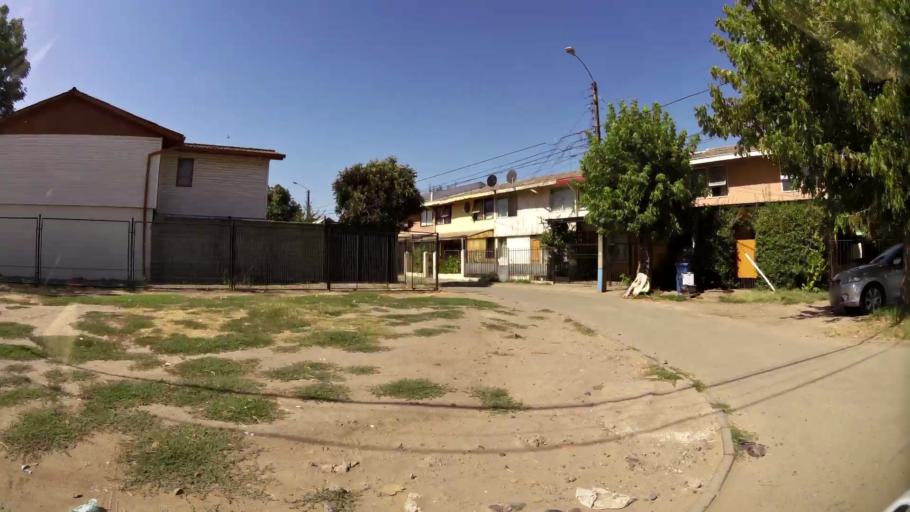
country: CL
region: Maule
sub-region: Provincia de Talca
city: Talca
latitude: -35.4368
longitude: -71.6601
